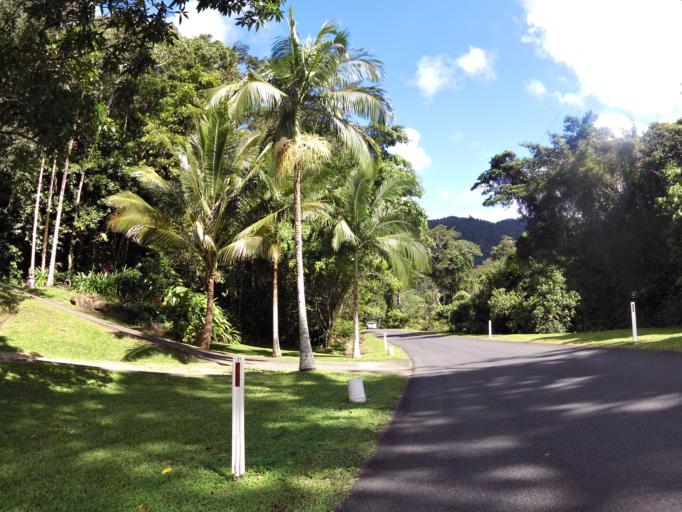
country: AU
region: Queensland
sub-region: Cairns
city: Woree
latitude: -16.9581
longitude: 145.6839
